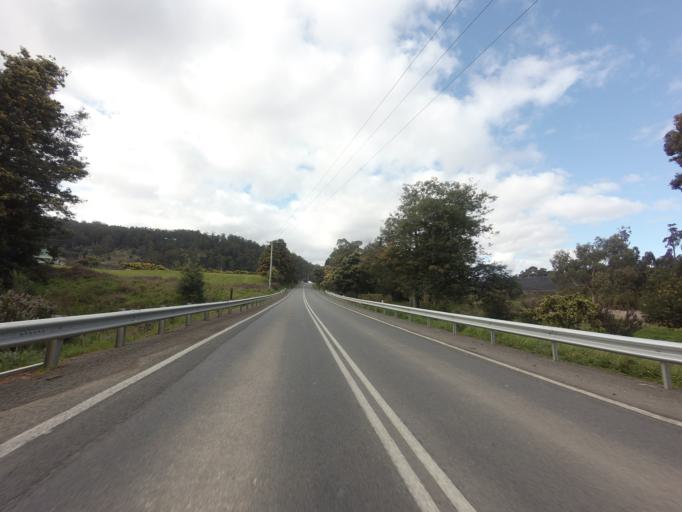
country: AU
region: Tasmania
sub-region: Huon Valley
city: Geeveston
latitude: -43.1376
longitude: 146.9725
